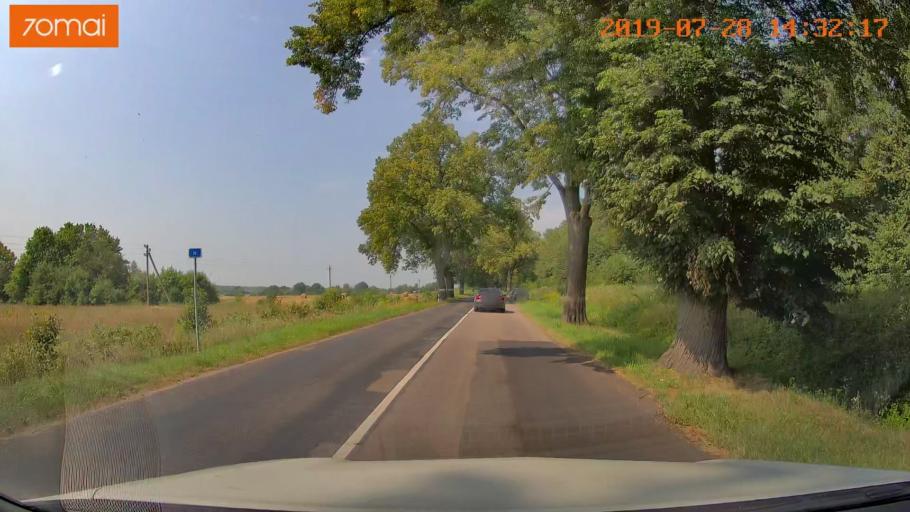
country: RU
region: Kaliningrad
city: Primorsk
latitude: 54.8117
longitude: 20.0431
